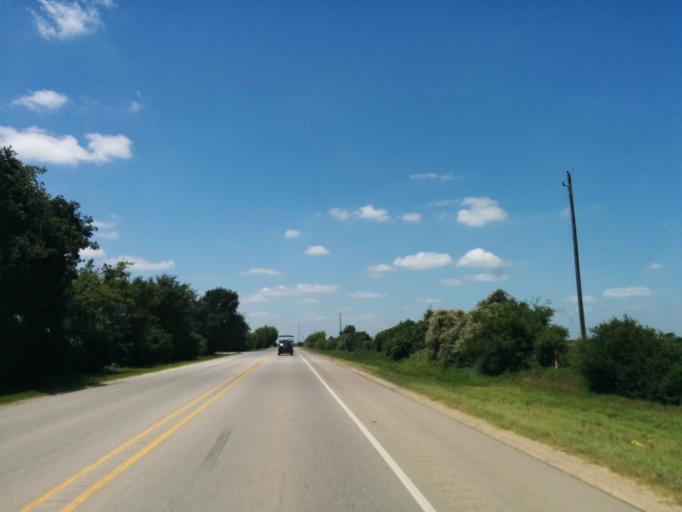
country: US
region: Texas
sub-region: Leon County
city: Hilltop Lakes
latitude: 30.8834
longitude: -96.1766
